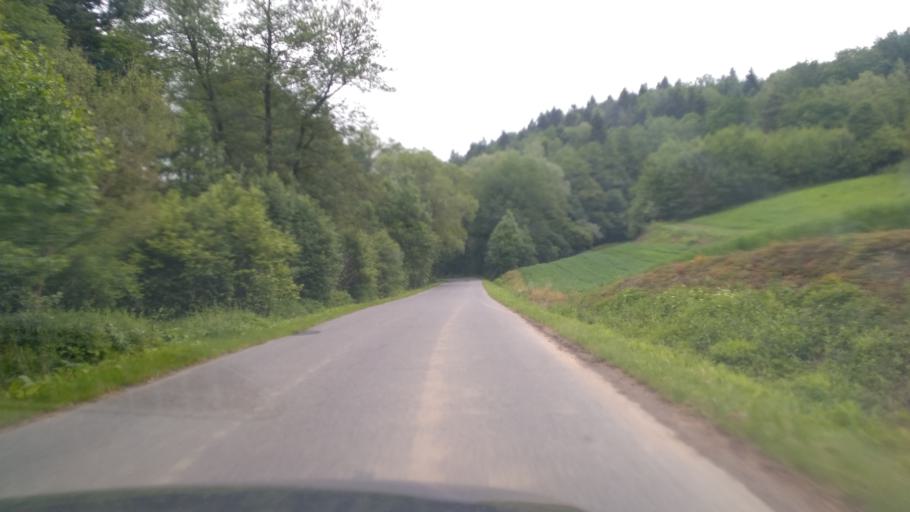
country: PL
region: Subcarpathian Voivodeship
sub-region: Powiat ropczycko-sedziszowski
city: Zagorzyce
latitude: 50.0048
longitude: 21.6812
